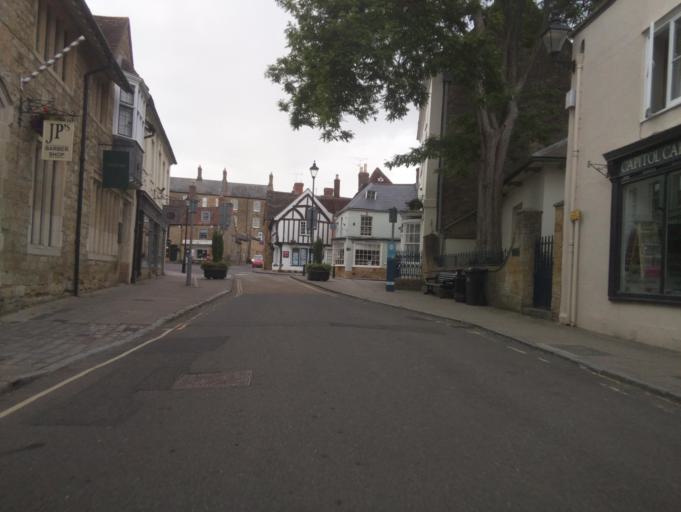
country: GB
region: England
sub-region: Dorset
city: Sherborne
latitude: 50.9497
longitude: -2.5168
